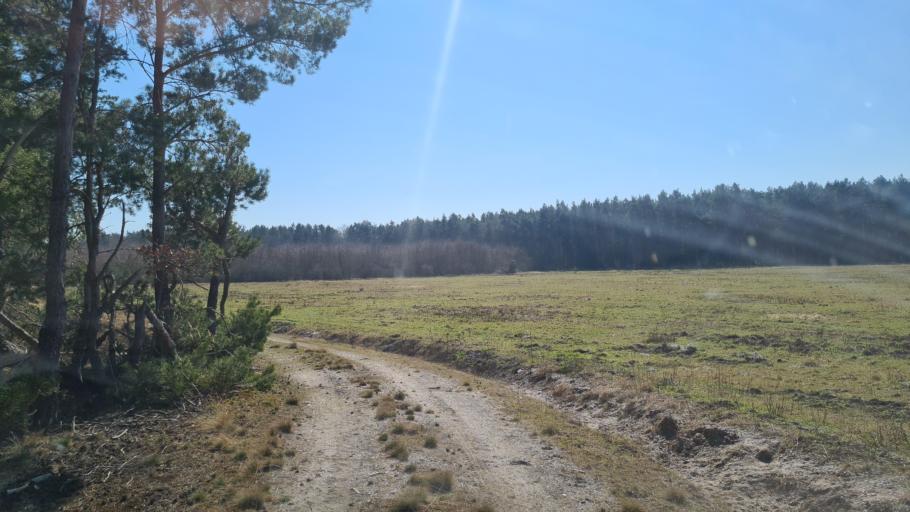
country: DE
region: Brandenburg
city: Finsterwalde
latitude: 51.5842
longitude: 13.7253
